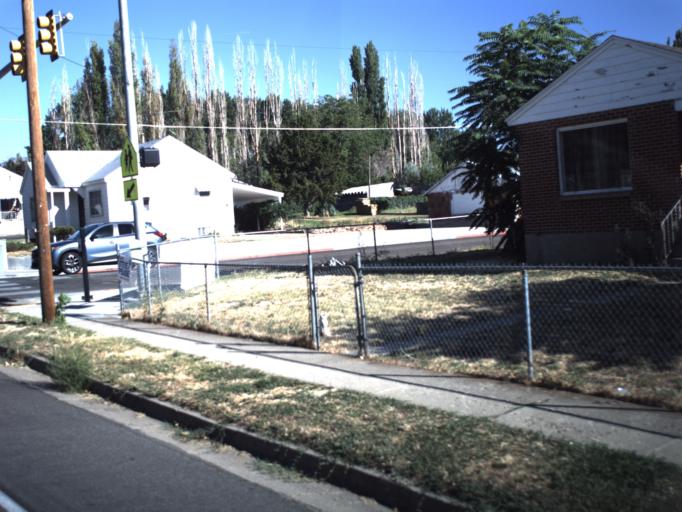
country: US
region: Utah
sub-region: Davis County
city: Sunset
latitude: 41.1398
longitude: -112.0312
